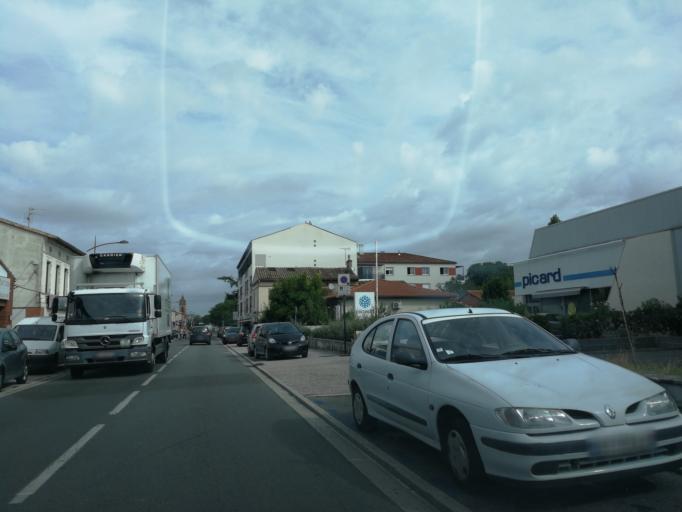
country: FR
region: Midi-Pyrenees
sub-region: Departement de la Haute-Garonne
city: Aucamville
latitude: 43.6625
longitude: 1.4311
